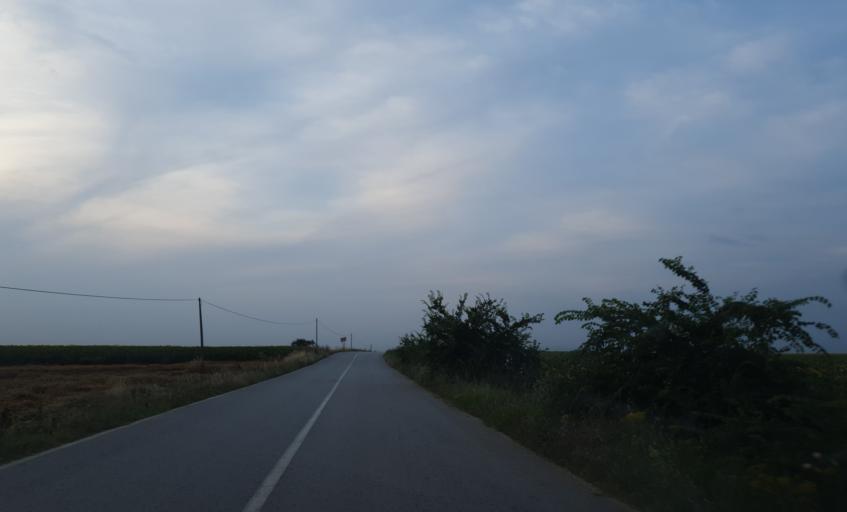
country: TR
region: Kirklareli
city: Buyukkaristiran
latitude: 41.3340
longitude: 27.6049
